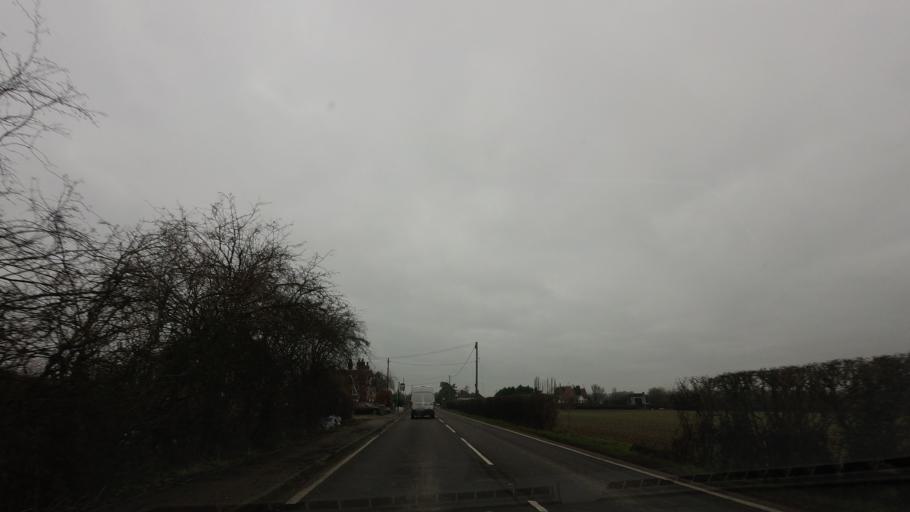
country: GB
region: England
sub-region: Kent
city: Staplehurst
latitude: 51.1364
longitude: 0.5562
